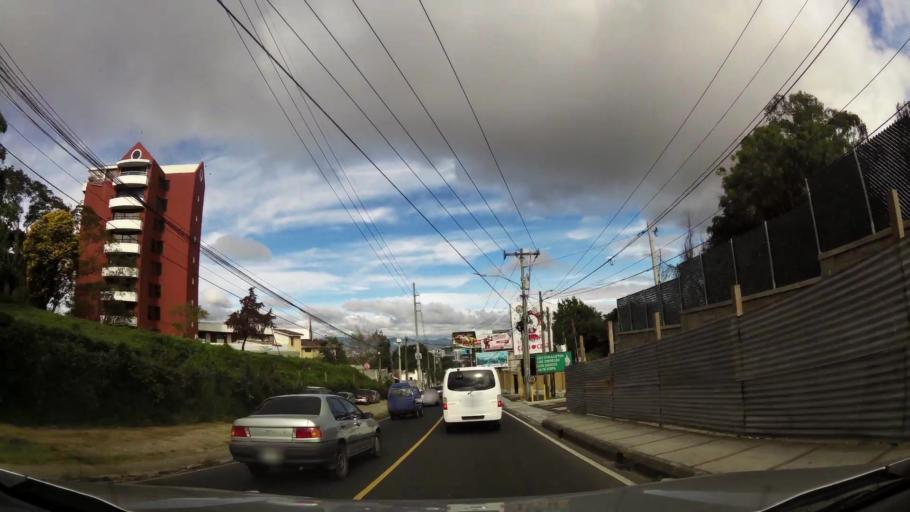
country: GT
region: Guatemala
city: Santa Catarina Pinula
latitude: 14.5747
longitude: -90.4898
